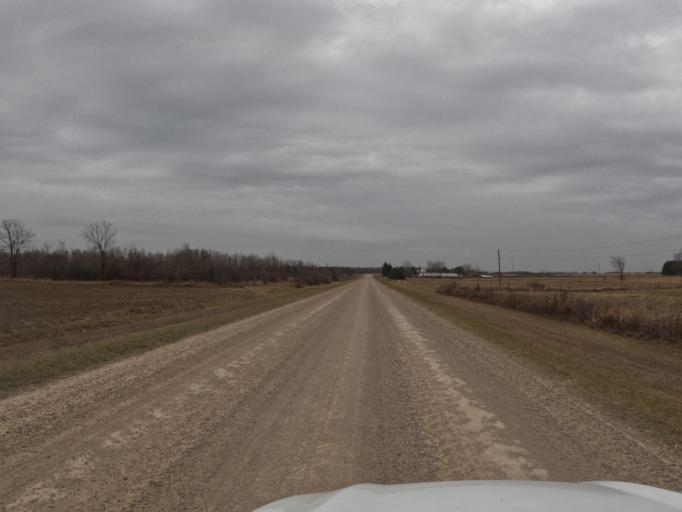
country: CA
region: Ontario
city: Shelburne
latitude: 43.8753
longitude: -80.3567
